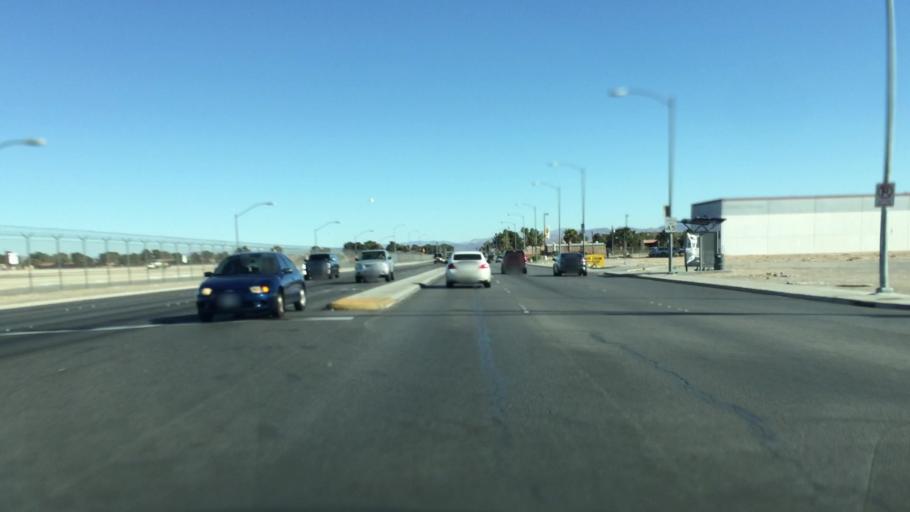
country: US
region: Nevada
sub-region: Clark County
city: Paradise
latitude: 36.0717
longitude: -115.1276
